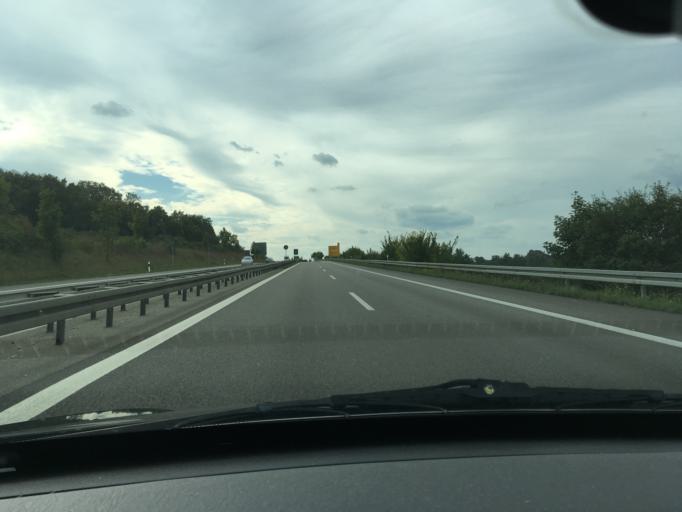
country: DE
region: Baden-Wuerttemberg
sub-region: Tuebingen Region
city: Dusslingen
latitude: 48.4675
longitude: 9.0636
